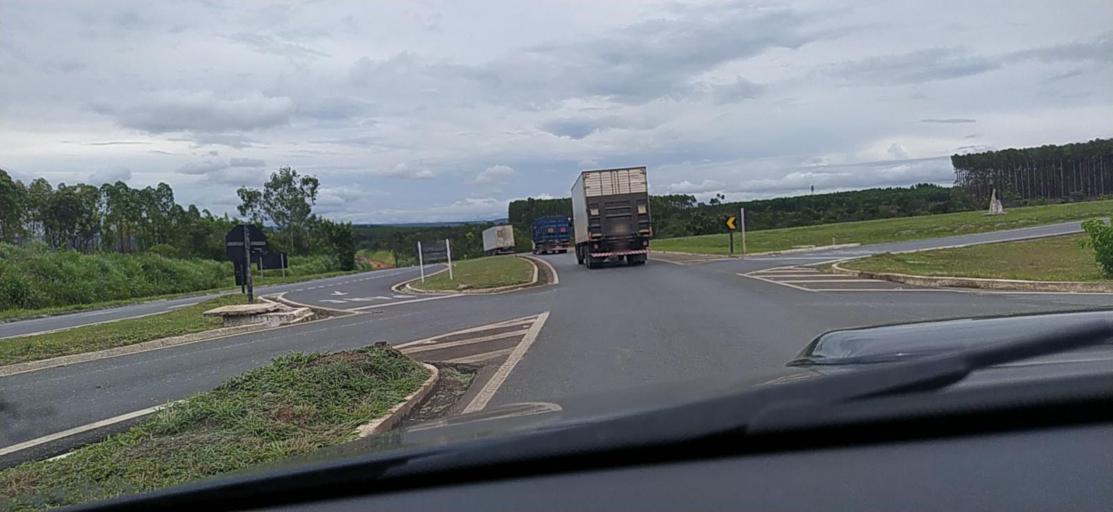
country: BR
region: Minas Gerais
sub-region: Curvelo
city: Curvelo
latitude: -18.7050
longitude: -44.4404
